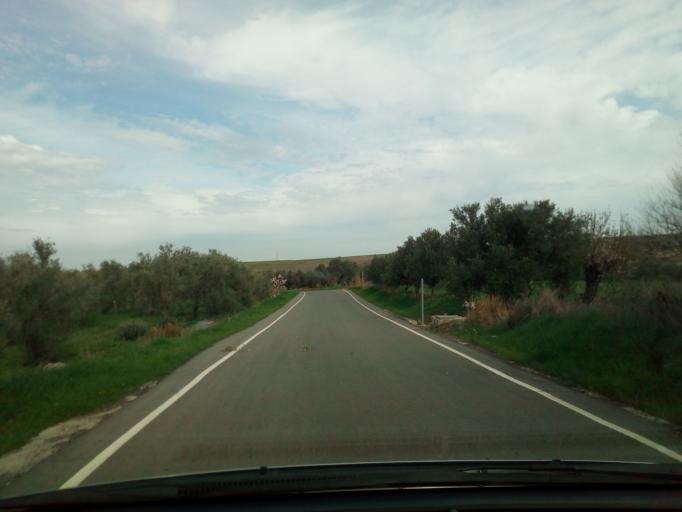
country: CY
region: Lefkosia
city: Astromeritis
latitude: 35.0886
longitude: 32.9950
